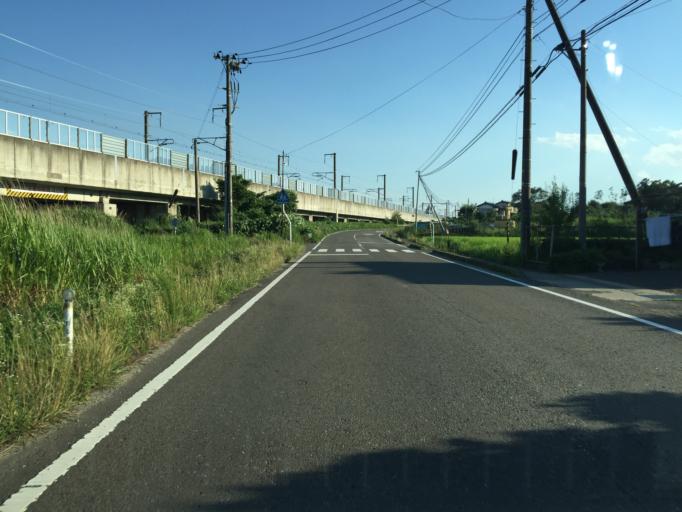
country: JP
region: Fukushima
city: Hobaramachi
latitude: 37.8625
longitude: 140.5223
